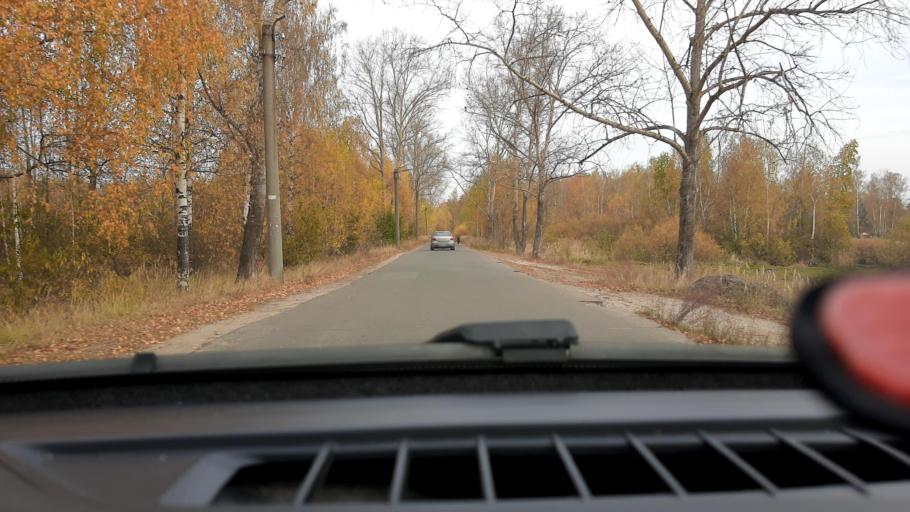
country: RU
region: Nizjnij Novgorod
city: Gorbatovka
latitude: 56.2920
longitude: 43.8320
